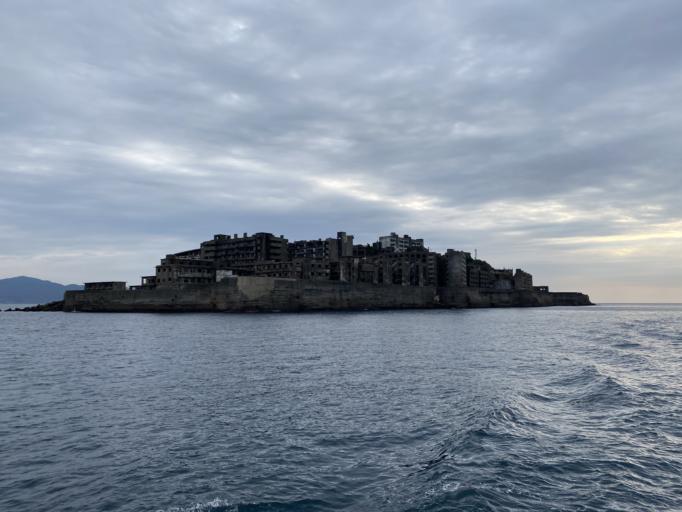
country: JP
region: Nagasaki
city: Nagasaki-shi
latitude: 32.6312
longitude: 129.7382
